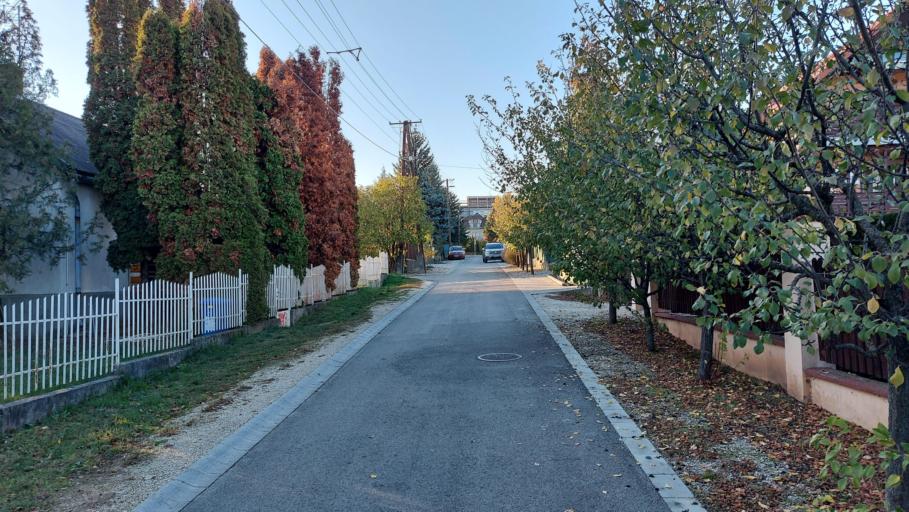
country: HU
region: Veszprem
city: Balatonalmadi
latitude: 47.0394
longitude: 18.0025
